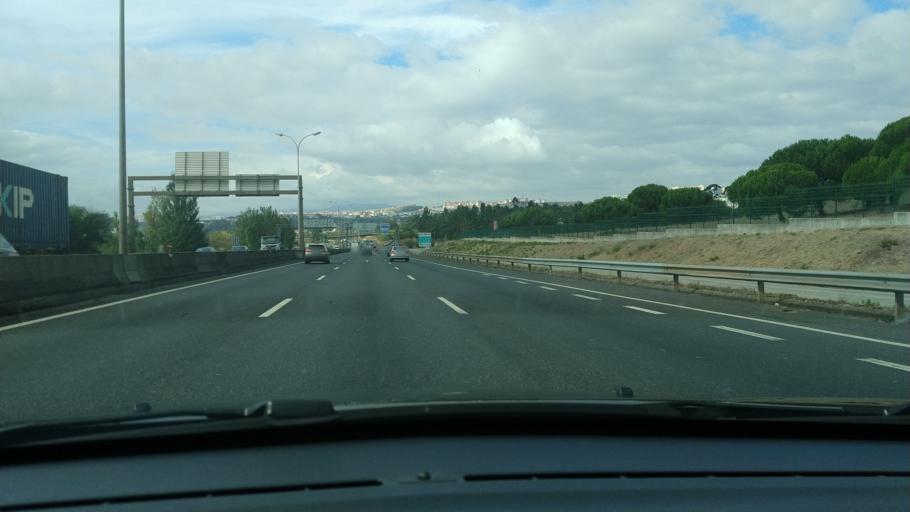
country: PT
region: Lisbon
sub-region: Amadora
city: Amadora
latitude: 38.7473
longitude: -9.2397
